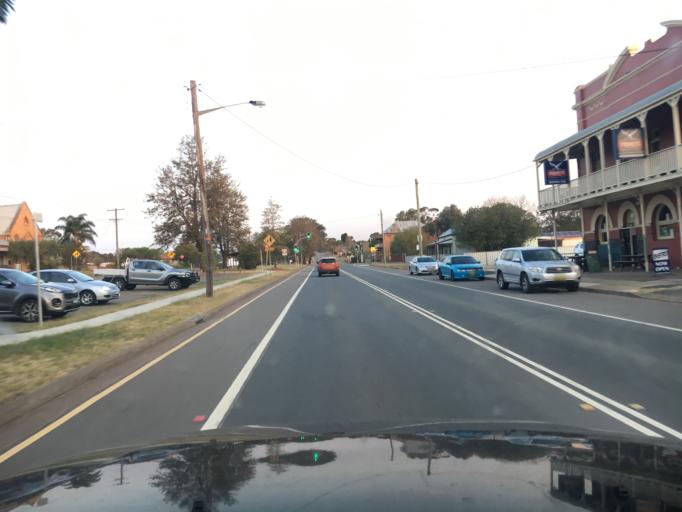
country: AU
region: New South Wales
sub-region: Cessnock
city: Greta
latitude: -32.6779
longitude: 151.3892
